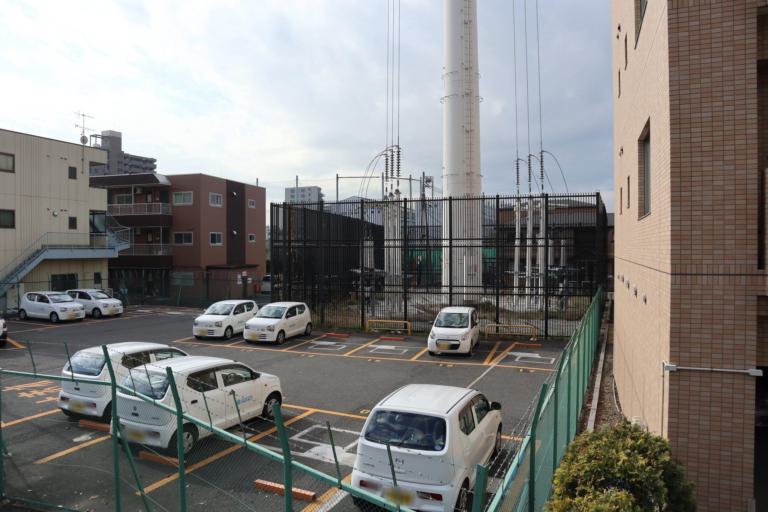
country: JP
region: Tokyo
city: Urayasu
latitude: 35.6844
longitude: 139.8816
